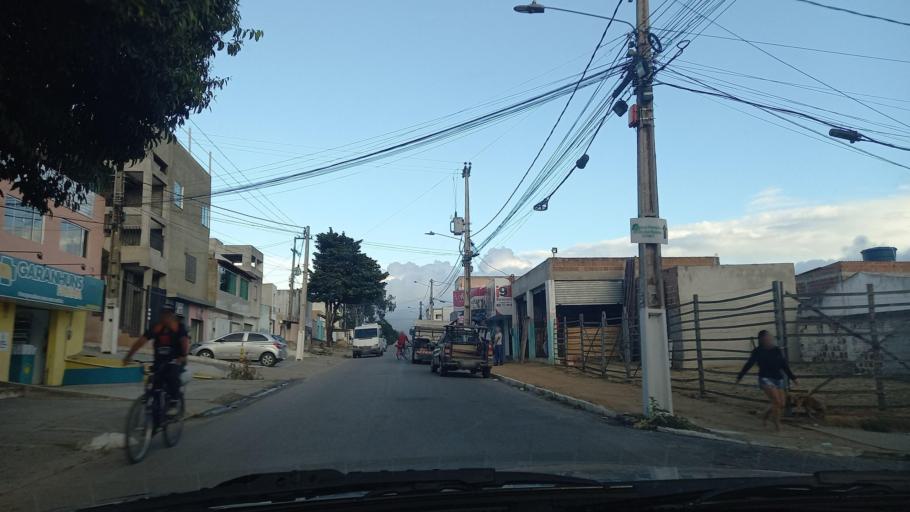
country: BR
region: Pernambuco
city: Garanhuns
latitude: -8.8868
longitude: -36.4628
